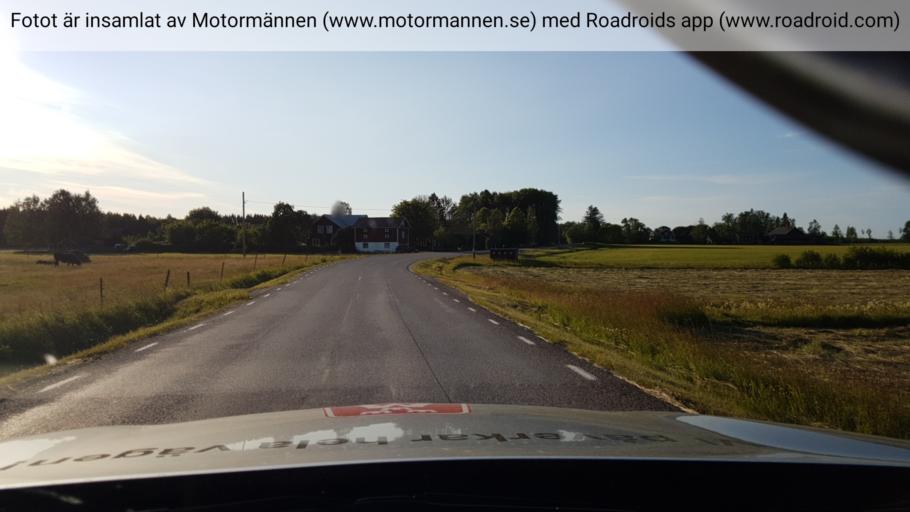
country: SE
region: Vaestmanland
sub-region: Surahammars Kommun
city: Ramnas
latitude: 59.9158
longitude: 16.3192
